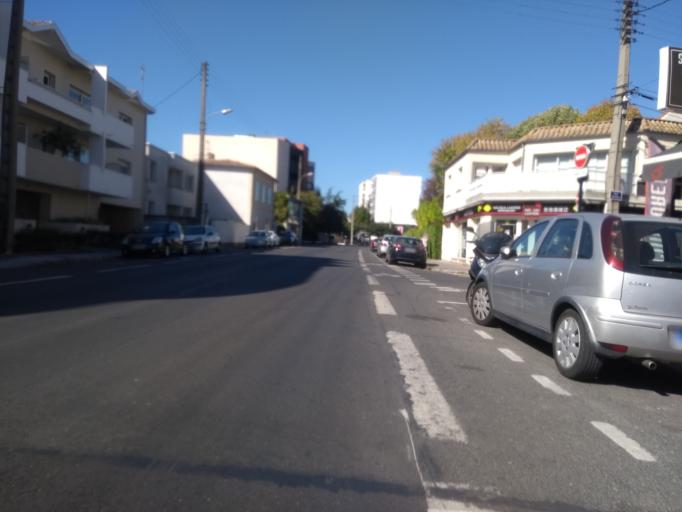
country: FR
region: Aquitaine
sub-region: Departement de la Gironde
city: Le Bouscat
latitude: 44.8438
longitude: -0.6084
